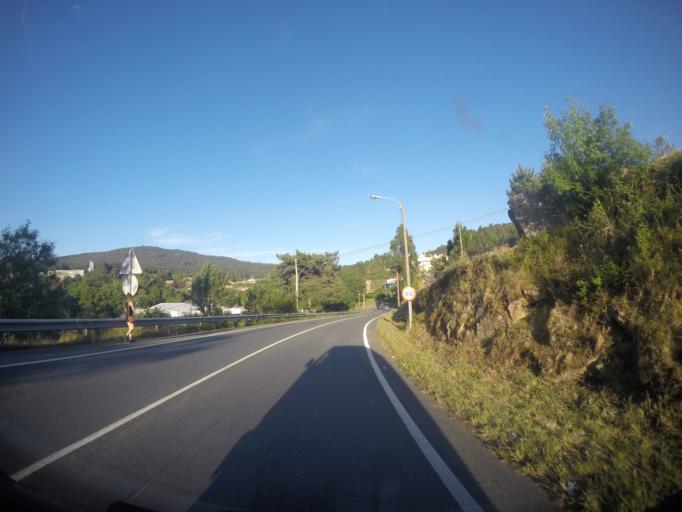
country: ES
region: Galicia
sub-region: Provincia da Coruna
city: Noia
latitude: 42.7657
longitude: -8.9401
